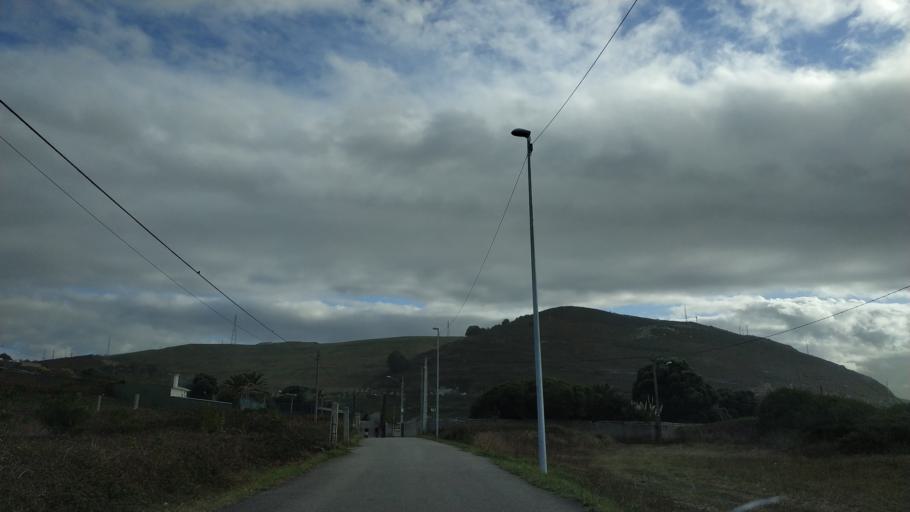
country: ES
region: Galicia
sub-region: Provincia da Coruna
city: A Coruna
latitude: 43.3760
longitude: -8.4464
